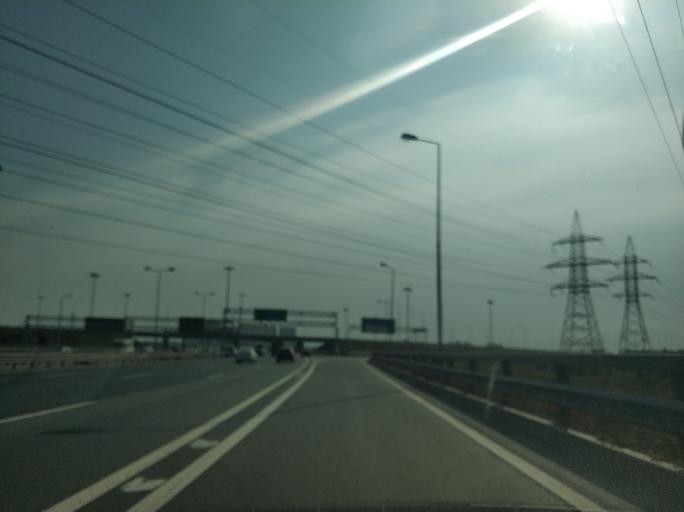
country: RU
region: Leningrad
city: Murino
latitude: 60.0191
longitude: 30.4569
